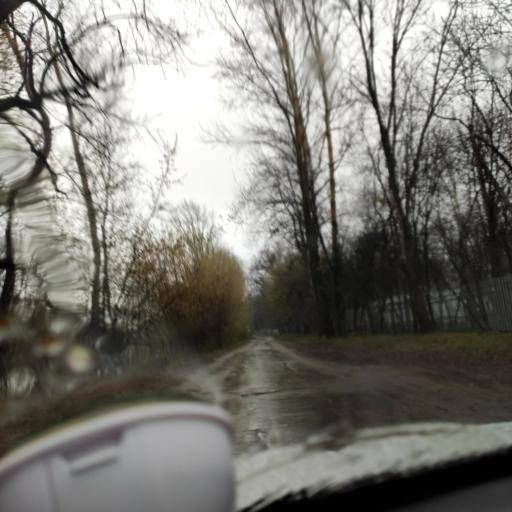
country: RU
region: Samara
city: Novokuybyshevsk
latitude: 53.1408
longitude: 49.9705
